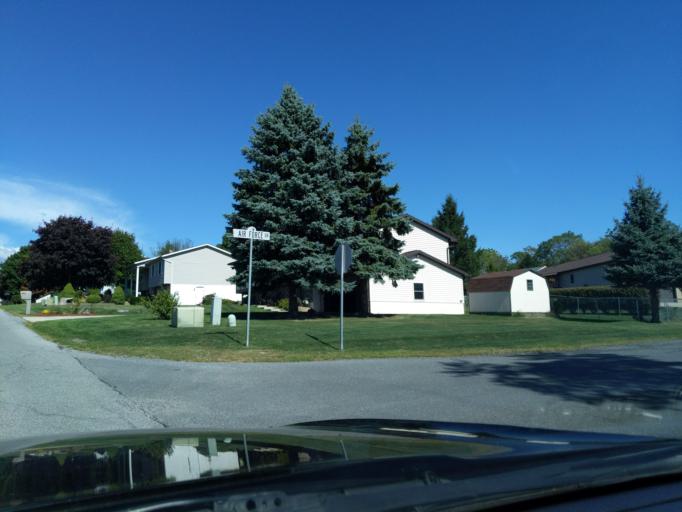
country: US
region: Pennsylvania
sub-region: Blair County
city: Greenwood
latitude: 40.5350
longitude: -78.3638
